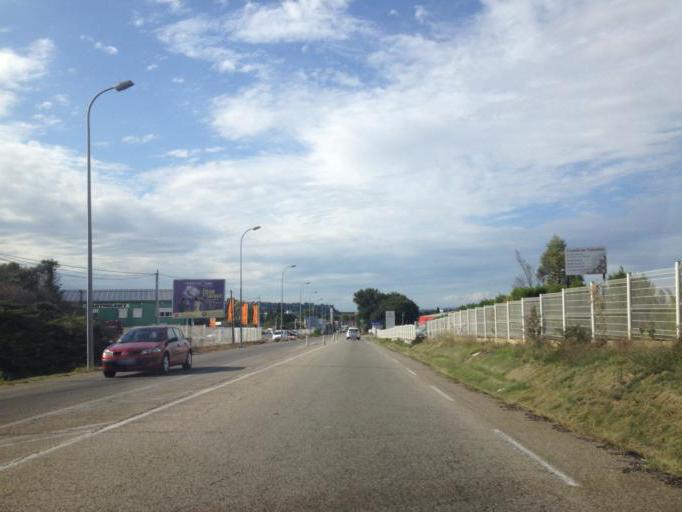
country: FR
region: Provence-Alpes-Cote d'Azur
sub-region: Departement du Vaucluse
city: Orange
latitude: 44.1209
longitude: 4.8326
